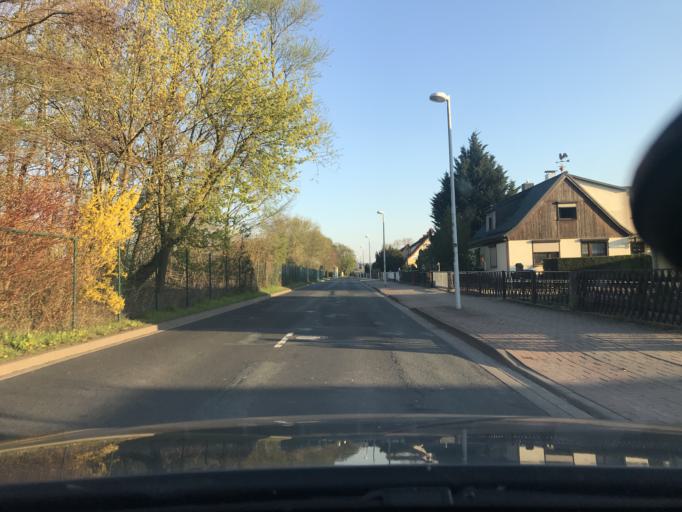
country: DE
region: Thuringia
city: Nordhausen
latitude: 51.4976
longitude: 10.7700
